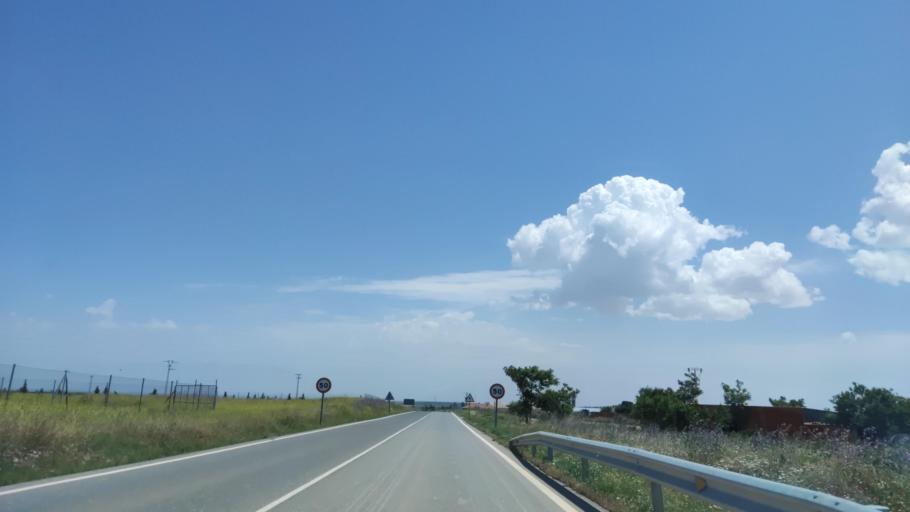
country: ES
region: Castille-La Mancha
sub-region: Province of Toledo
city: Mascaraque
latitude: 39.7166
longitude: -3.8203
